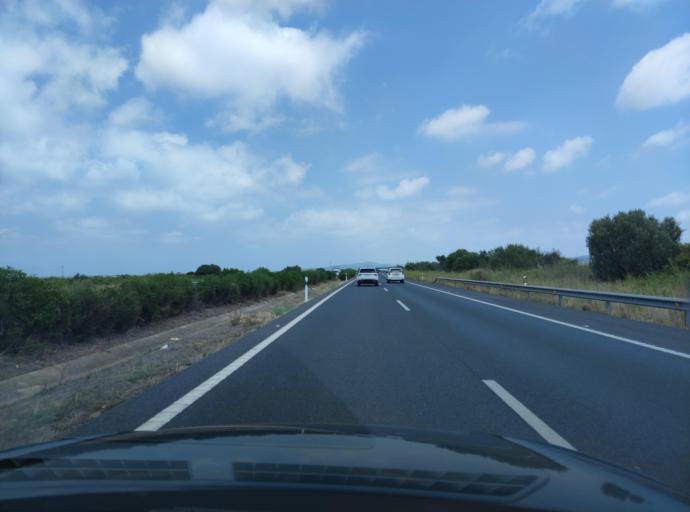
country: ES
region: Catalonia
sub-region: Provincia de Tarragona
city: Alcanar
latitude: 40.5181
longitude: 0.4158
